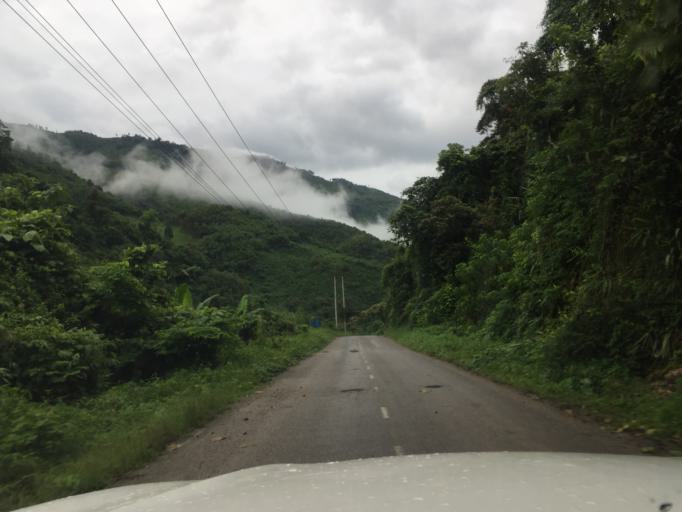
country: LA
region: Oudomxai
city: Muang La
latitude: 21.0093
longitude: 102.2334
